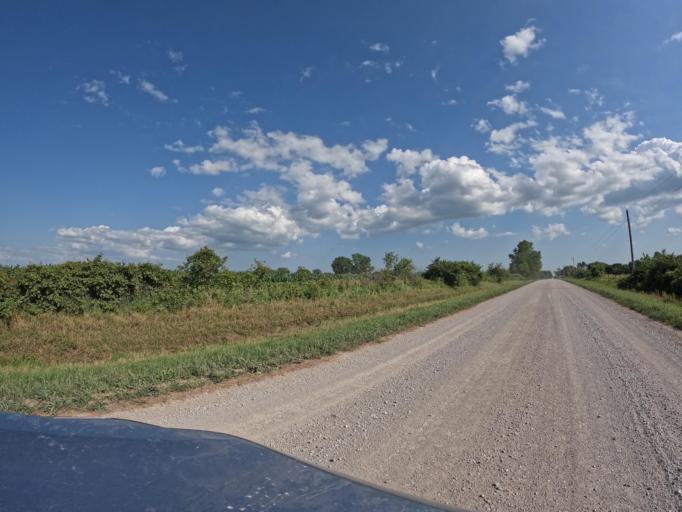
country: US
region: Iowa
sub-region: Appanoose County
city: Centerville
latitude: 40.7234
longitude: -93.0301
